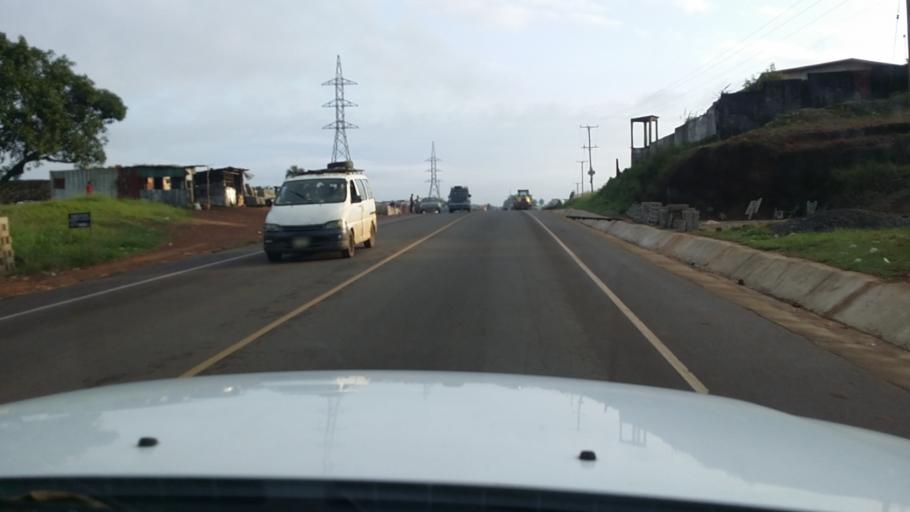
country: LR
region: Montserrado
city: Monrovia
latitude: 6.3215
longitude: -10.6641
